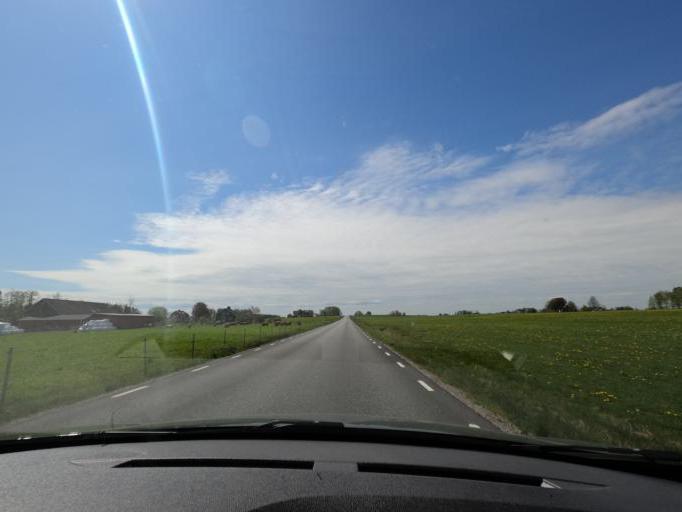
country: SE
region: Joenkoeping
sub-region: Varnamo Kommun
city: Bredaryd
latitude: 57.1481
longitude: 13.7254
